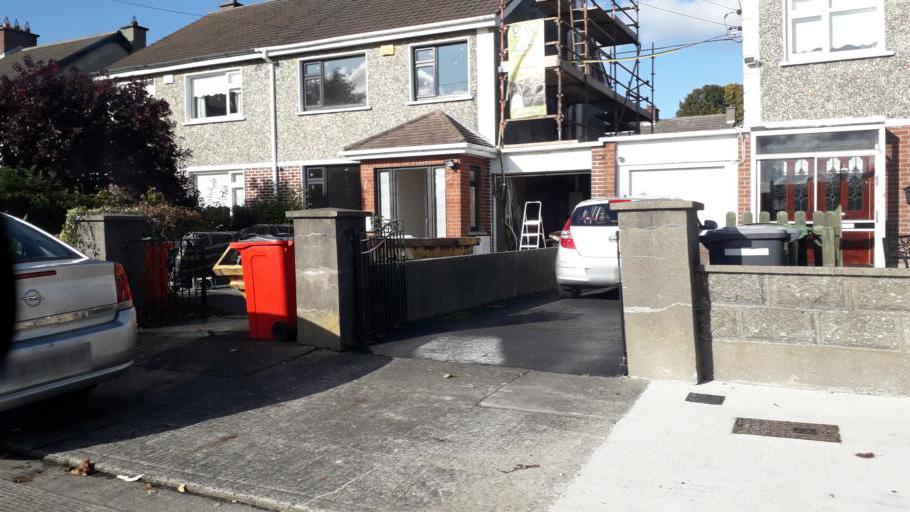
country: IE
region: Leinster
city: Raheny
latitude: 53.3899
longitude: -6.1852
